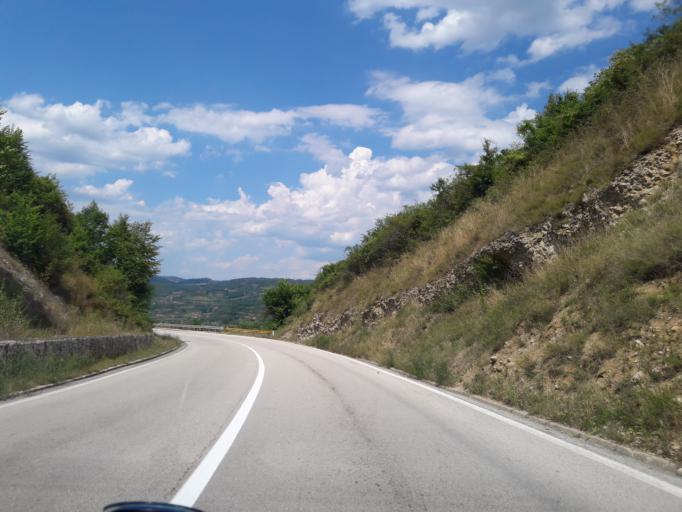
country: BA
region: Republika Srpska
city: Mrkonjic Grad
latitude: 44.5084
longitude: 17.1561
